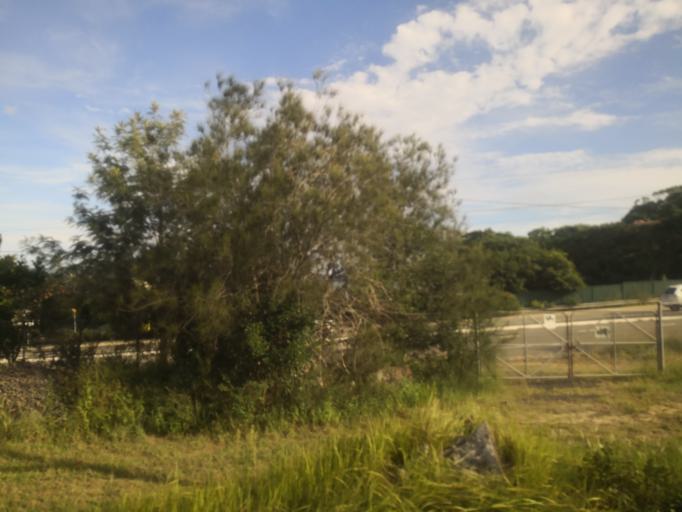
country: AU
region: New South Wales
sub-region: Gosford Shire
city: Point Clare
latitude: -33.4501
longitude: 151.3205
